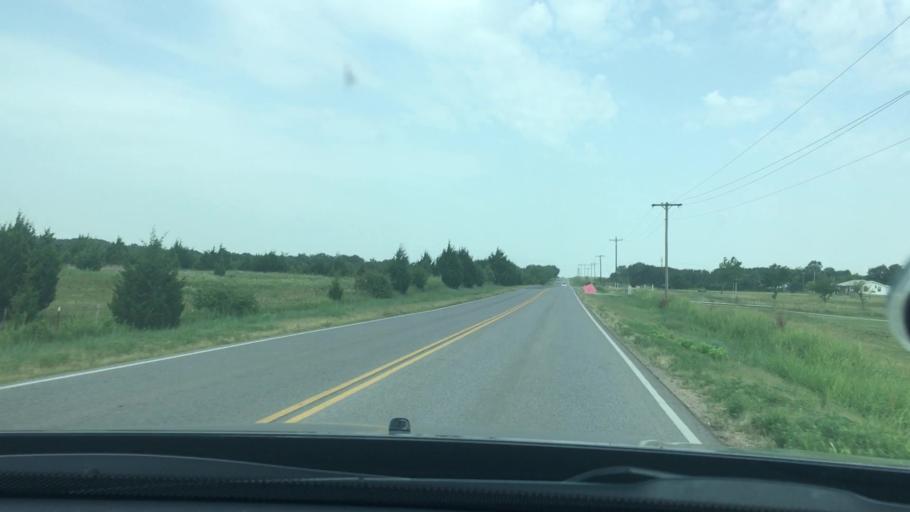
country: US
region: Oklahoma
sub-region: Garvin County
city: Stratford
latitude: 34.7967
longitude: -96.8980
